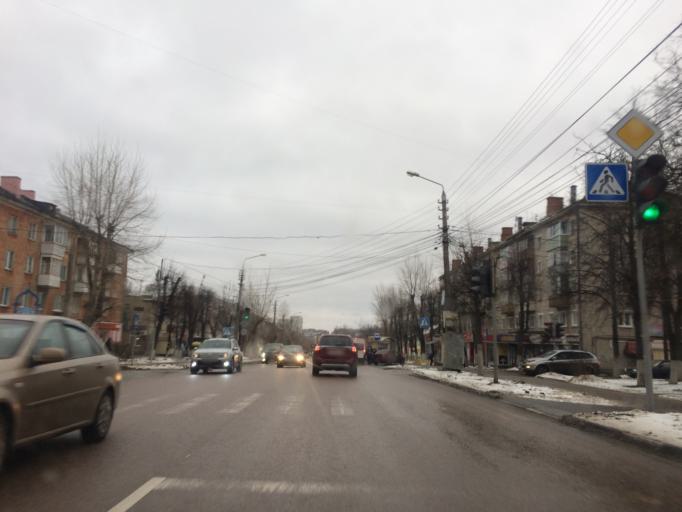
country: RU
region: Tula
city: Tula
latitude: 54.2099
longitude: 37.6701
